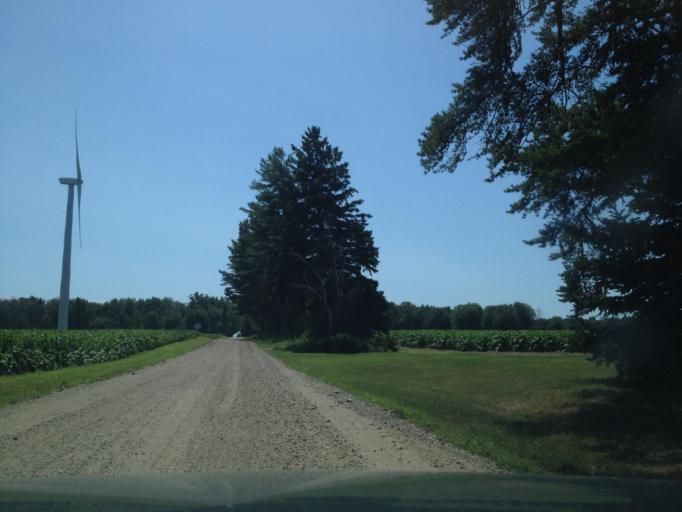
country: CA
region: Ontario
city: Aylmer
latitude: 42.6510
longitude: -80.7704
